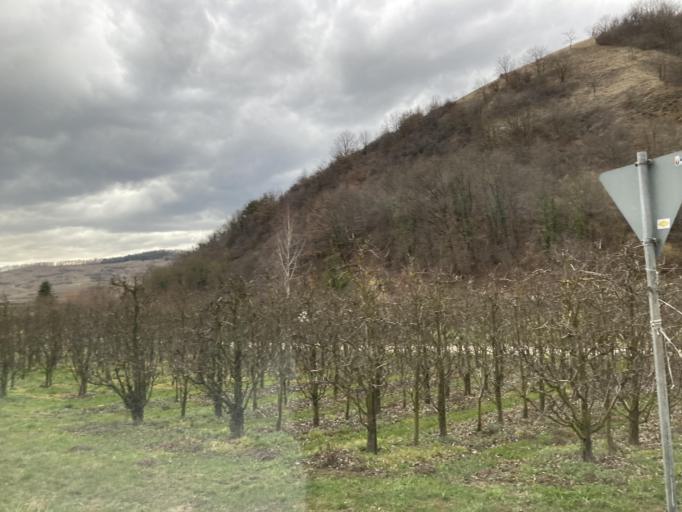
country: DE
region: Baden-Wuerttemberg
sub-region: Freiburg Region
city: Vogtsburg
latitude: 48.0918
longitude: 7.6730
